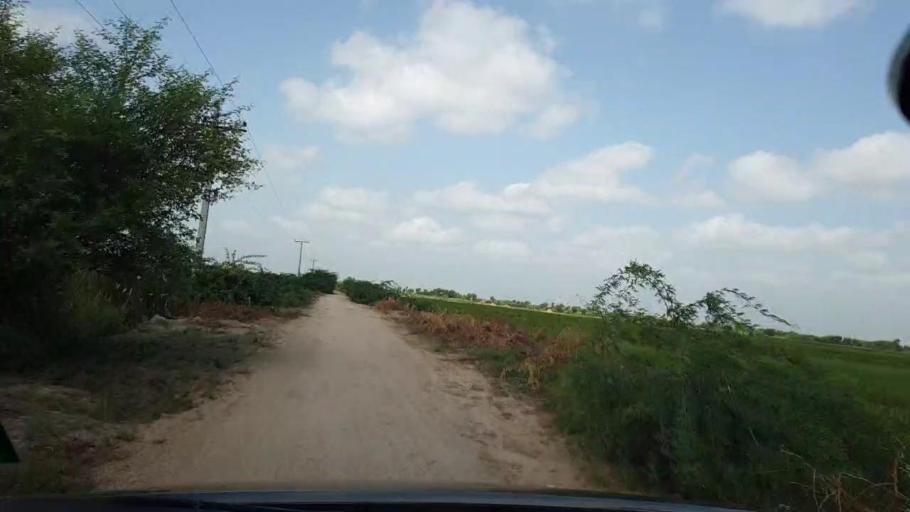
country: PK
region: Sindh
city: Kadhan
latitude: 24.6191
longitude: 69.1097
